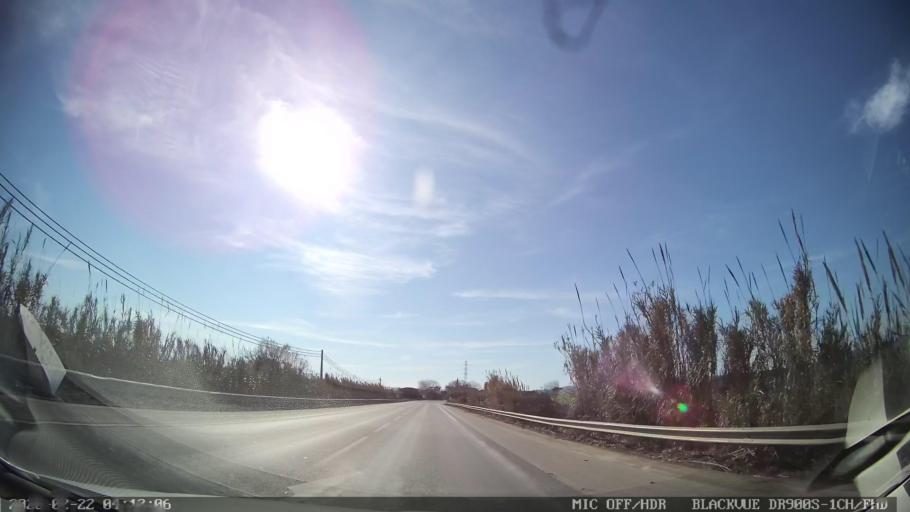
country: PT
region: Lisbon
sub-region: Alenquer
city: Carregado
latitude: 39.0329
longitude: -8.9421
